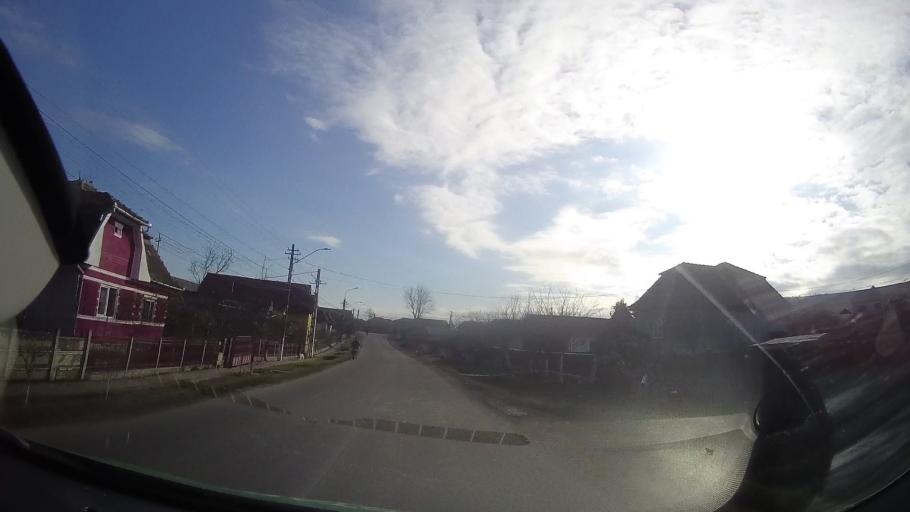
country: RO
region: Mures
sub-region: Comuna Valea Larga
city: Valea Larga
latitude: 46.6172
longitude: 24.0808
